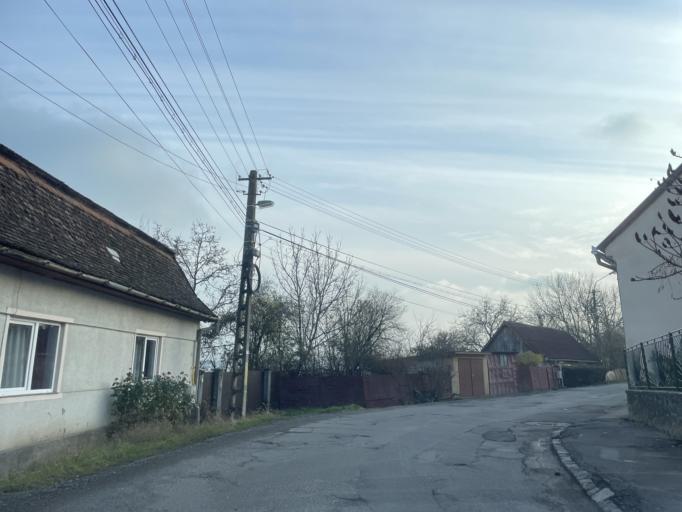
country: RO
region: Mures
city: Reghin-Sat
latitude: 46.7835
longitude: 24.7065
